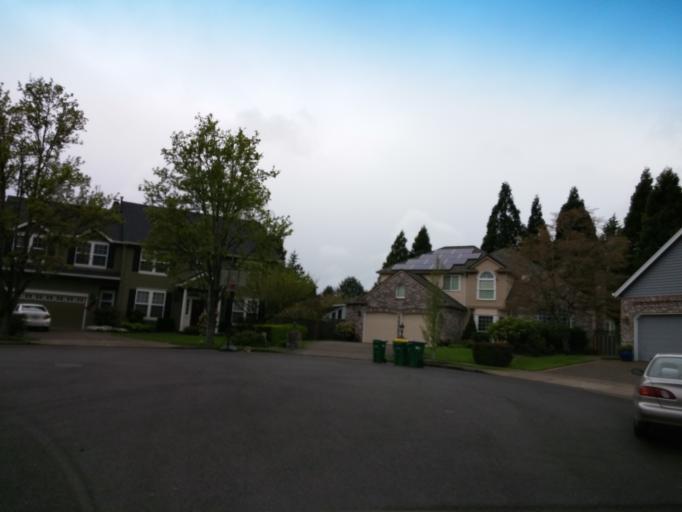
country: US
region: Oregon
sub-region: Washington County
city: Oak Hills
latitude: 45.5233
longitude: -122.8504
